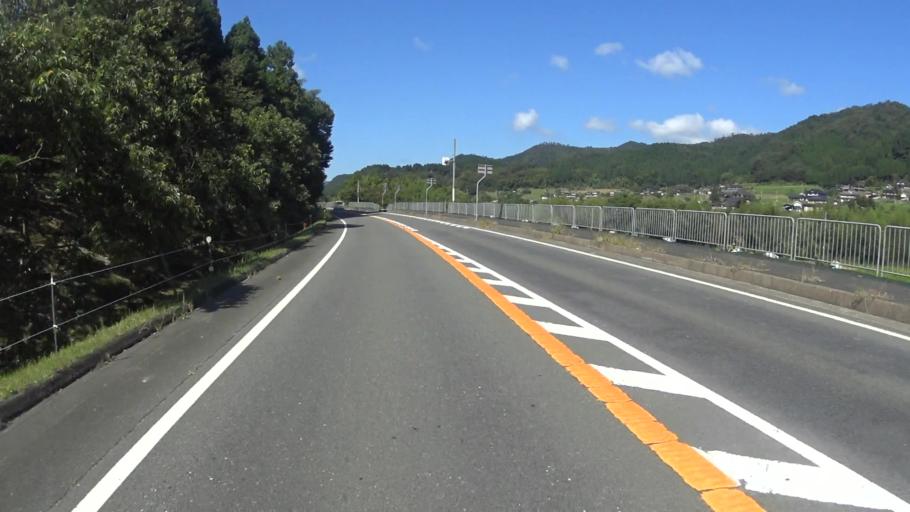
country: JP
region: Kyoto
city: Ayabe
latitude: 35.2700
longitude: 135.3954
